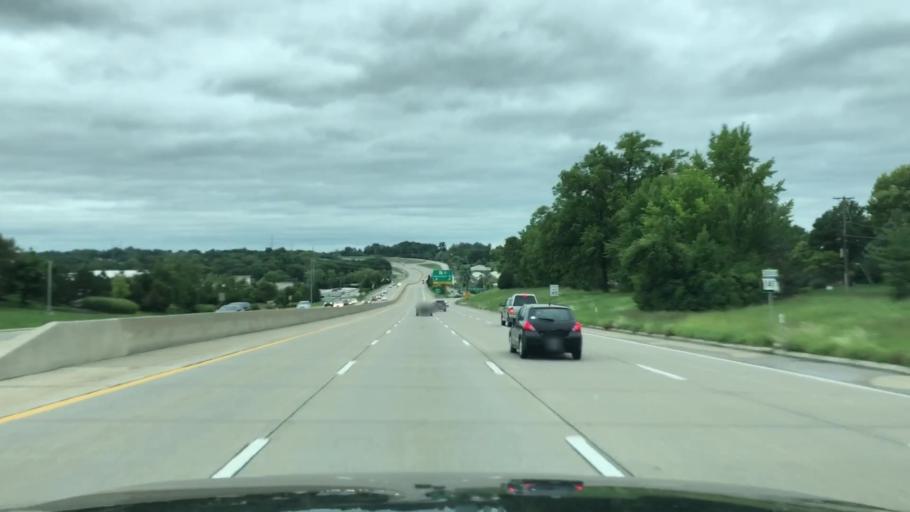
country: US
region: Missouri
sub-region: Saint Louis County
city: Manchester
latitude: 38.5979
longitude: -90.5088
